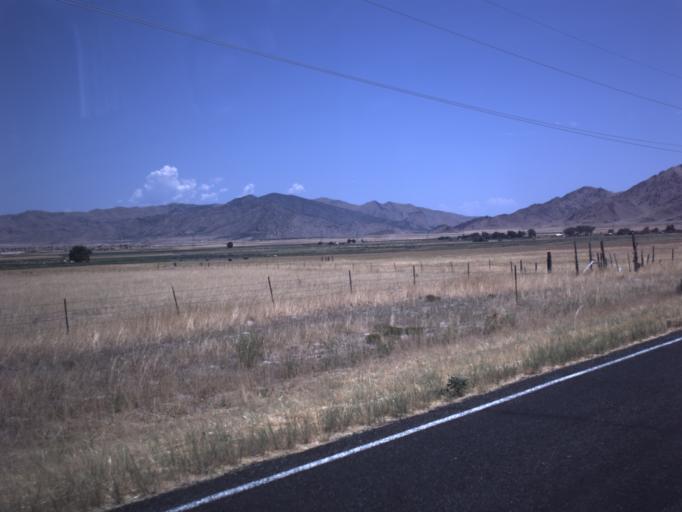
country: US
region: Utah
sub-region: Millard County
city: Delta
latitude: 39.4640
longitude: -112.2839
